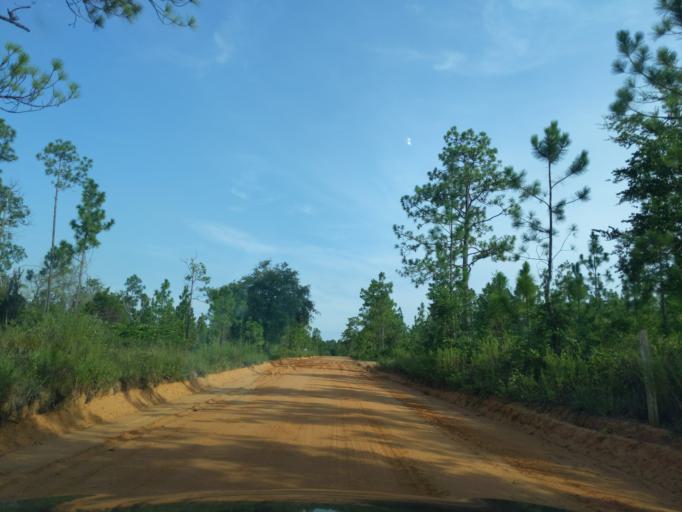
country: US
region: Florida
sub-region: Gadsden County
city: Midway
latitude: 30.3994
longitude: -84.4109
